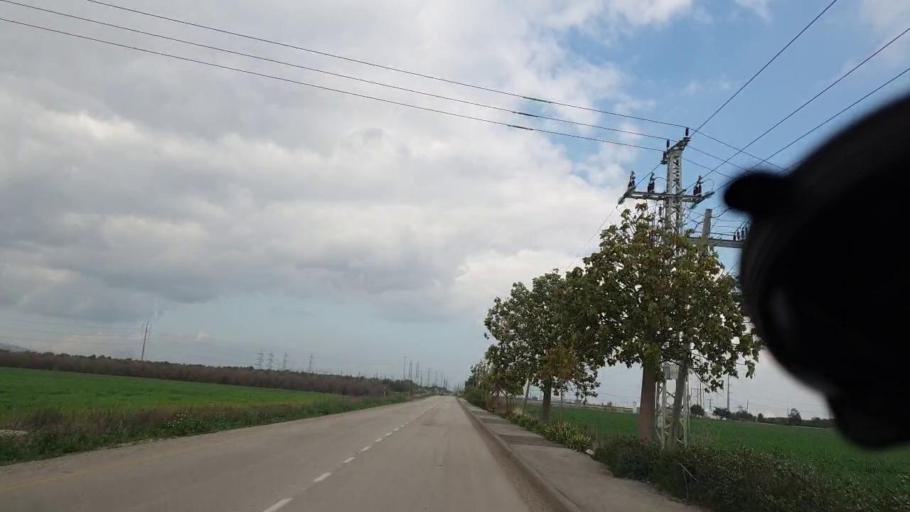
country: IL
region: Haifa
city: Rekhasim
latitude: 32.7523
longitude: 35.0870
